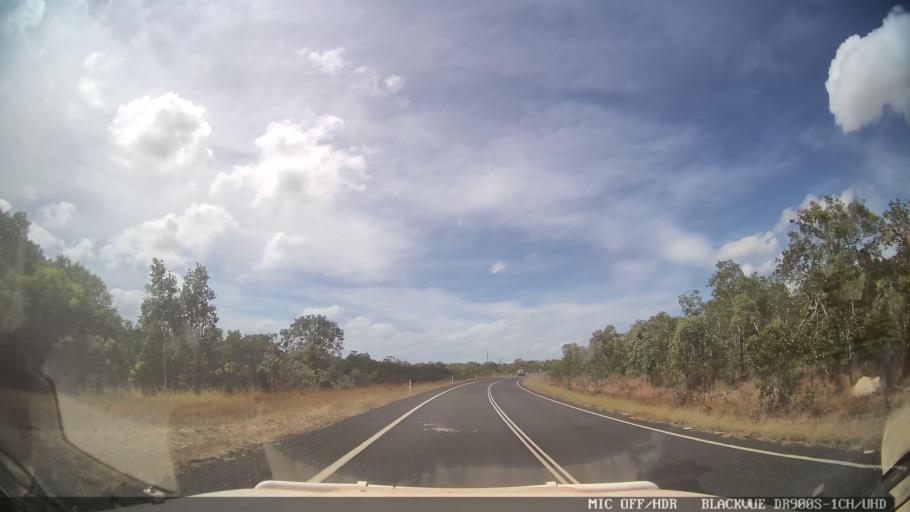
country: AU
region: Queensland
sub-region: Cook
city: Cooktown
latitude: -15.5361
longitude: 145.2364
